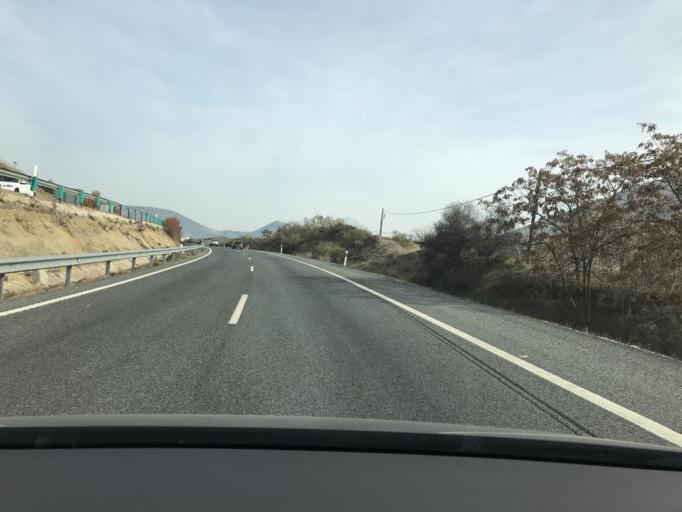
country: ES
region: Andalusia
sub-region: Provincia de Granada
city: Loja
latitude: 37.1585
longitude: -4.1991
